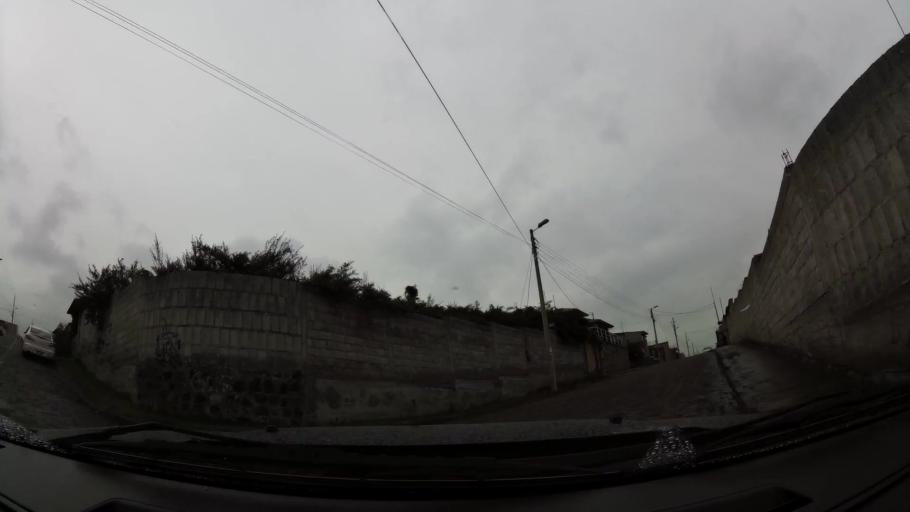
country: EC
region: Pichincha
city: Sangolqui
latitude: -0.3208
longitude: -78.4314
